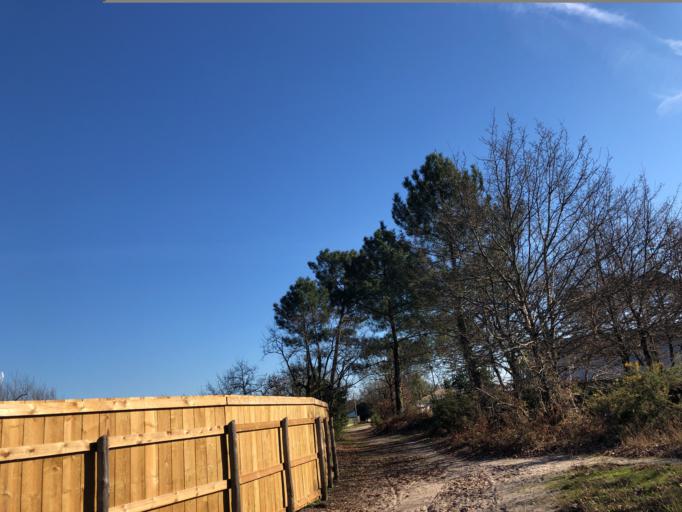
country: FR
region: Aquitaine
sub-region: Departement de la Gironde
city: Andernos-les-Bains
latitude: 44.7512
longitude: -1.0904
